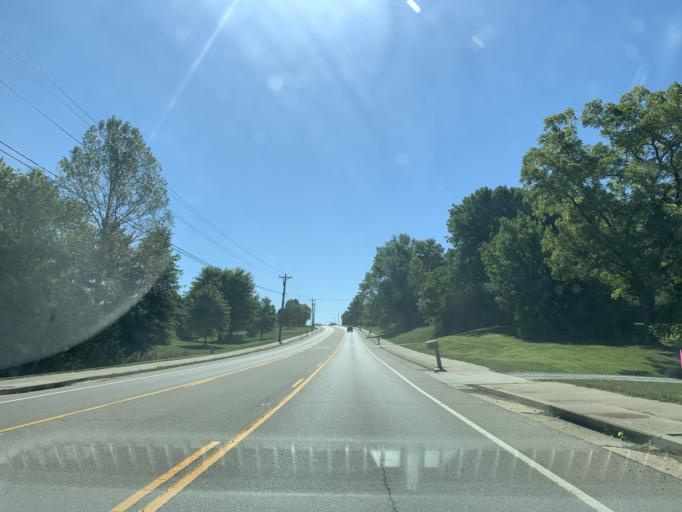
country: US
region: Kentucky
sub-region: Boone County
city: Francisville
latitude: 39.1025
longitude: -84.7223
